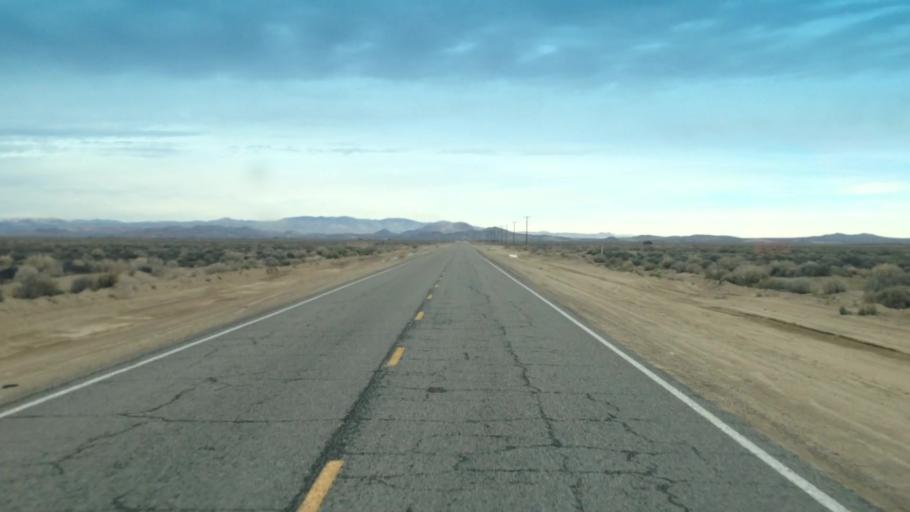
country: US
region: California
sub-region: Los Angeles County
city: Lancaster
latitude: 34.7527
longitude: -118.1844
